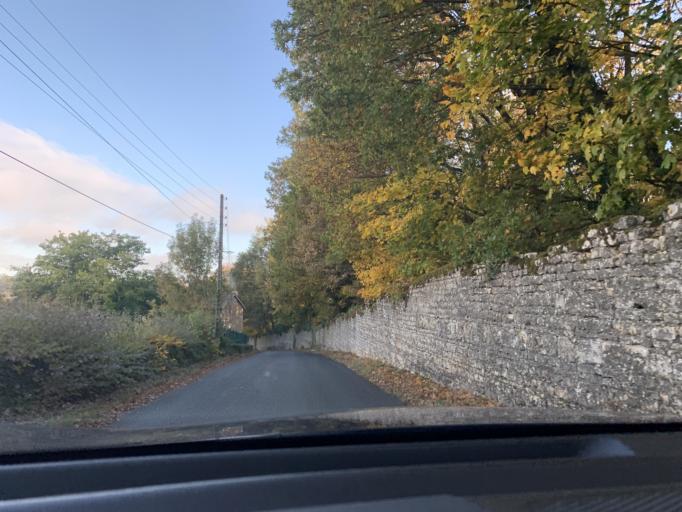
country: FR
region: Rhone-Alpes
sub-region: Departement du Rhone
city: Pommiers
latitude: 45.9525
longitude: 4.7002
